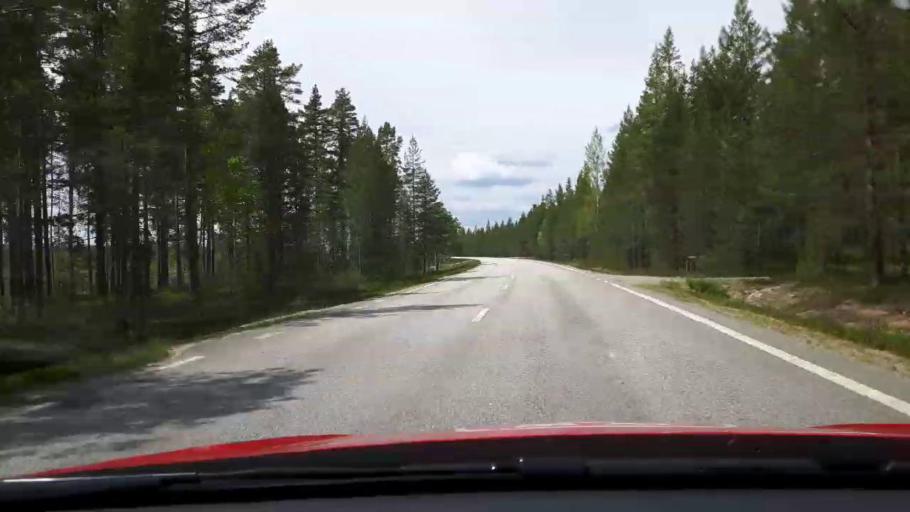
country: SE
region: Jaemtland
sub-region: Harjedalens Kommun
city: Sveg
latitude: 62.1360
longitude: 14.0437
